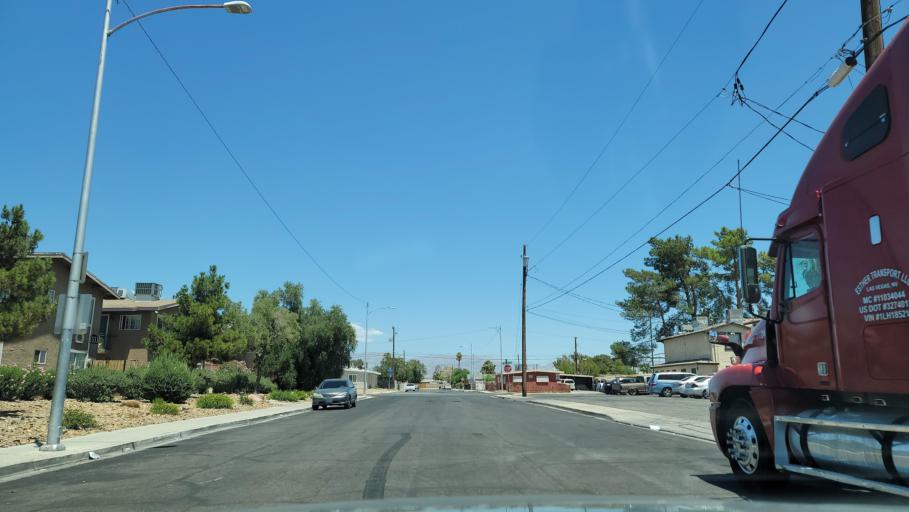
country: US
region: Nevada
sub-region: Clark County
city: North Las Vegas
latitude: 36.1877
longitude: -115.1184
